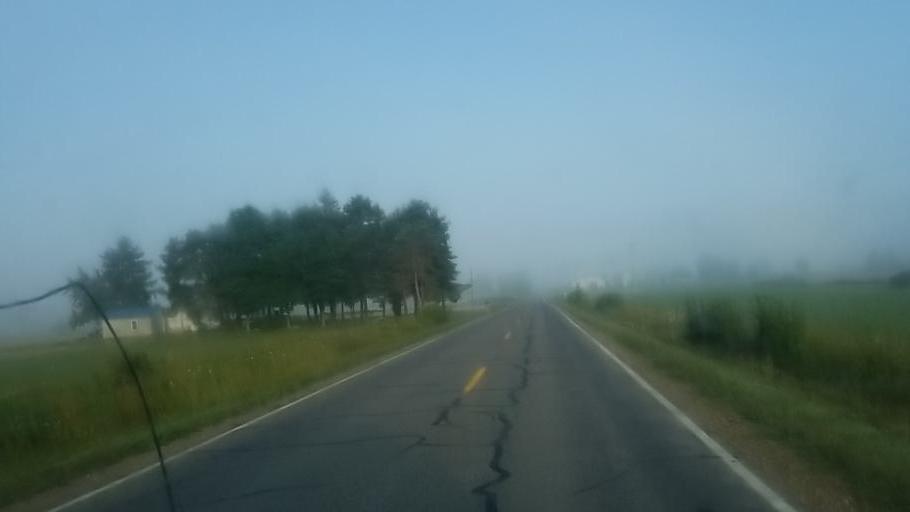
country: US
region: Michigan
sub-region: Newaygo County
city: Fremont
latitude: 43.4678
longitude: -86.0731
